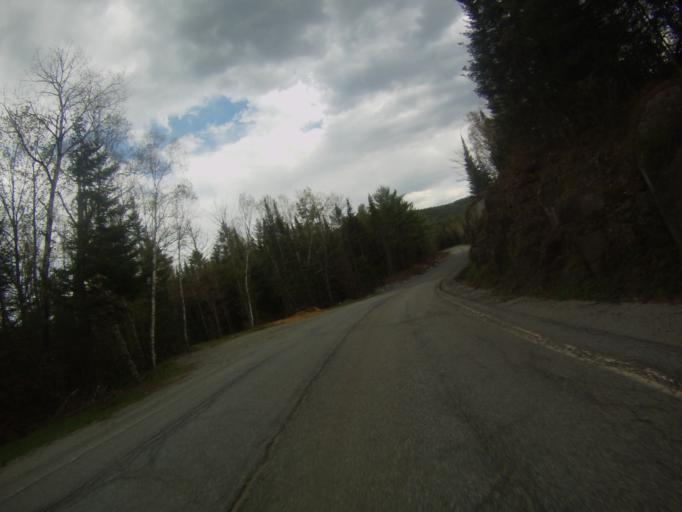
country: US
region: New York
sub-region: Essex County
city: Mineville
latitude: 44.0810
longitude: -73.6101
